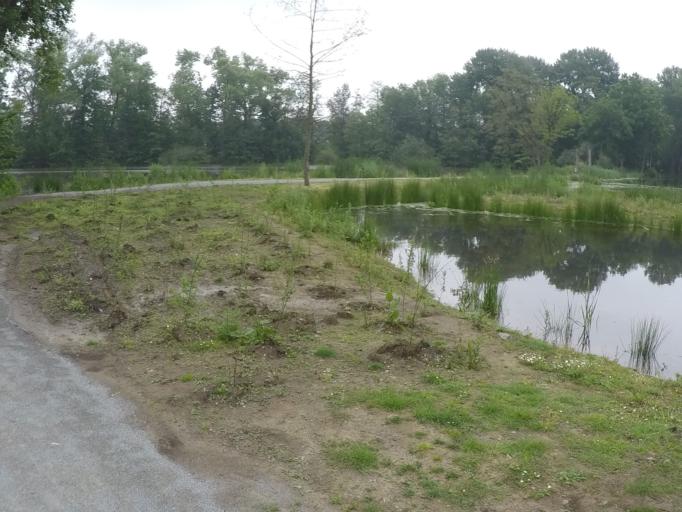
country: BE
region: Flanders
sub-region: Provincie Oost-Vlaanderen
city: Berlare
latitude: 51.0394
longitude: 3.9766
